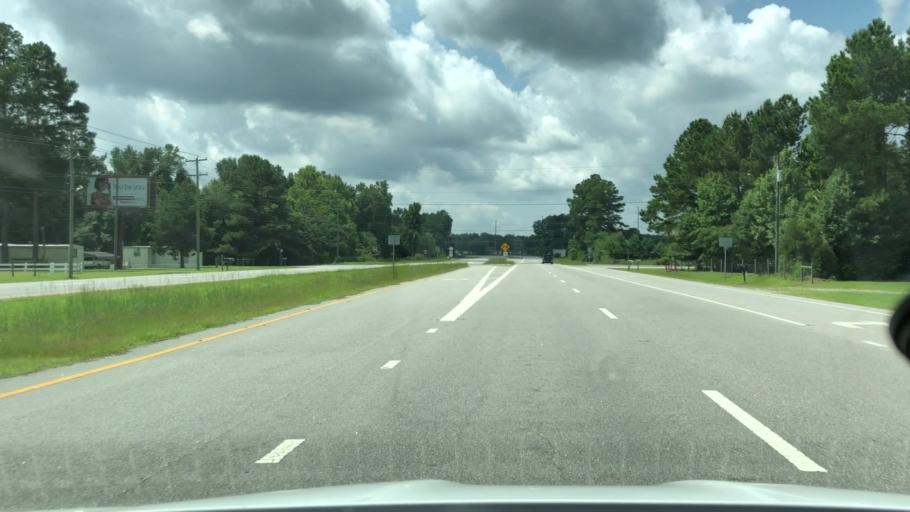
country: US
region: North Carolina
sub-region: Beaufort County
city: Washington
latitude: 35.4799
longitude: -77.1147
